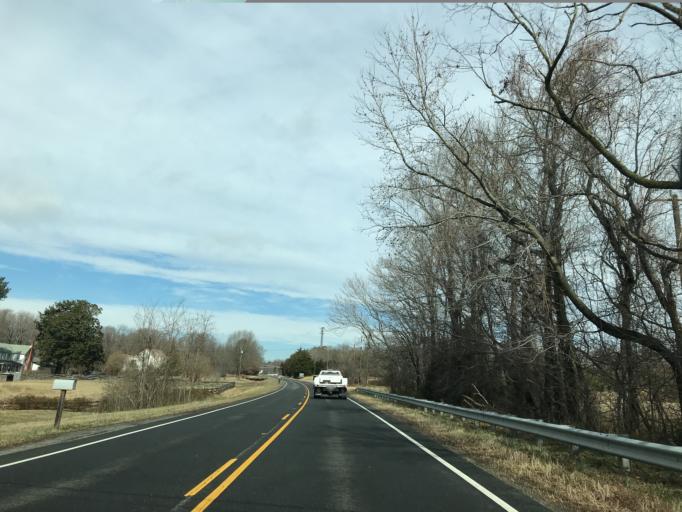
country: US
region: Virginia
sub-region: King George County
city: Dahlgren
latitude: 38.3311
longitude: -77.0828
